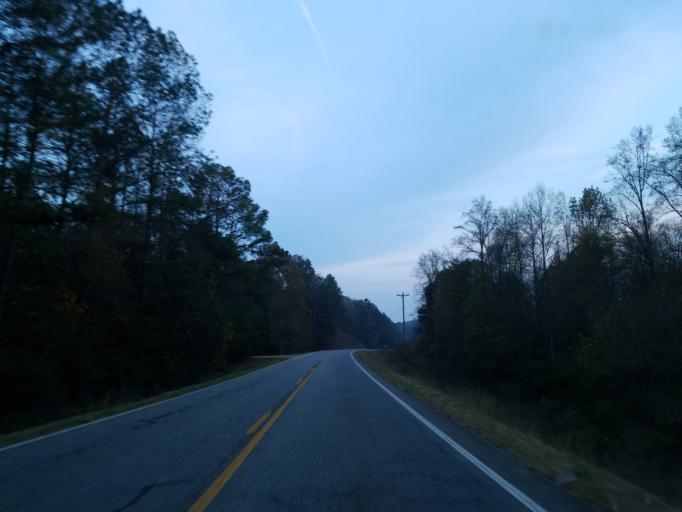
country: US
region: Georgia
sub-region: Gilmer County
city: Ellijay
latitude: 34.5694
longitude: -84.6115
